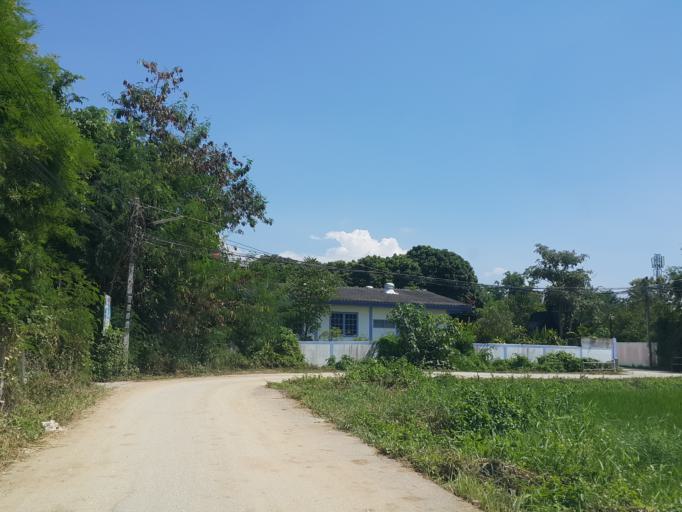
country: TH
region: Chiang Mai
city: Saraphi
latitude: 18.7615
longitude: 99.0513
